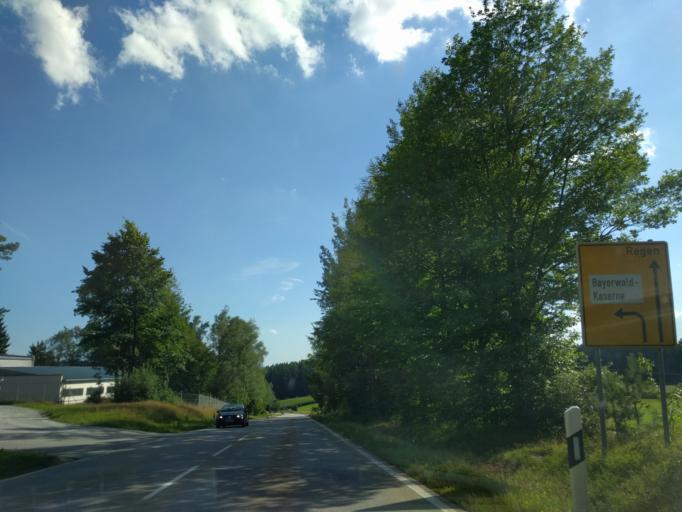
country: DE
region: Bavaria
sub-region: Lower Bavaria
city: Regen
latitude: 48.9911
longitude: 13.1353
